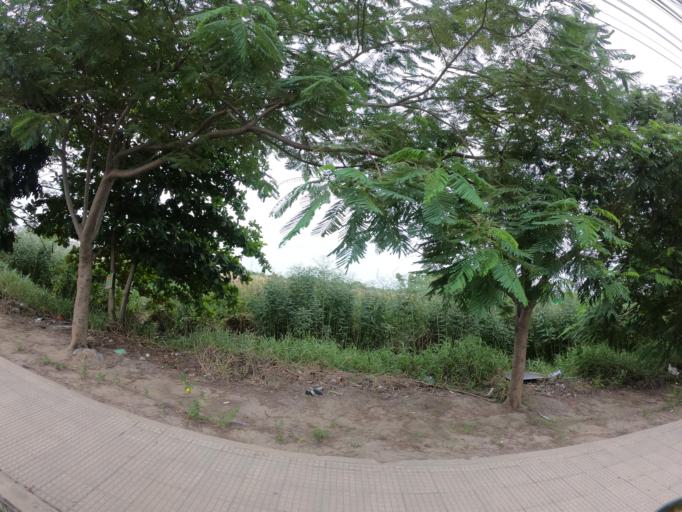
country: TH
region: Bangkok
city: Bang Na
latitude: 13.6625
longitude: 100.6819
